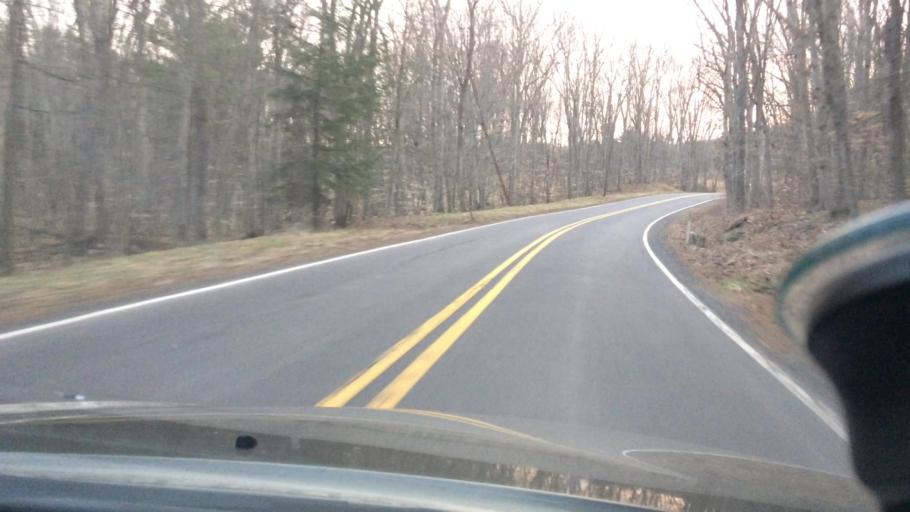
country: US
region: Pennsylvania
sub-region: Luzerne County
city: Freeland
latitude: 41.0752
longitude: -75.9133
